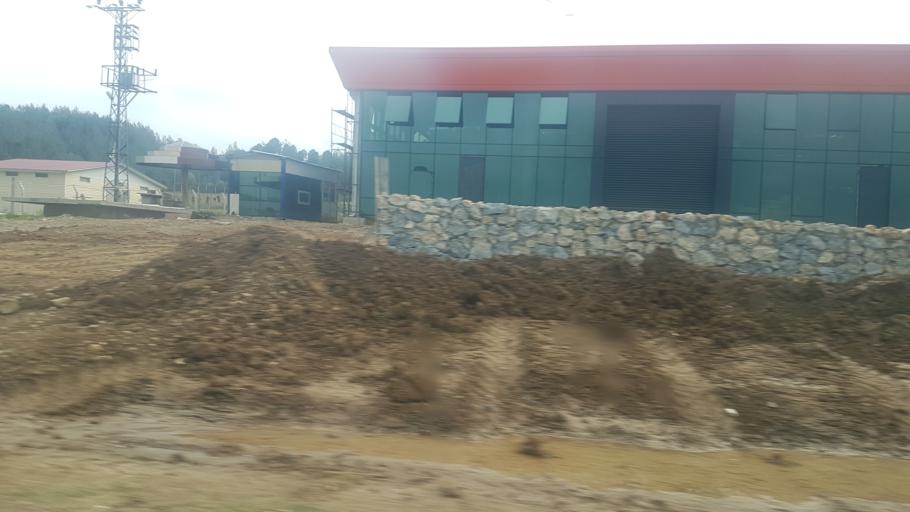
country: TR
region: Mersin
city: Yenice
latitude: 37.0918
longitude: 35.1480
